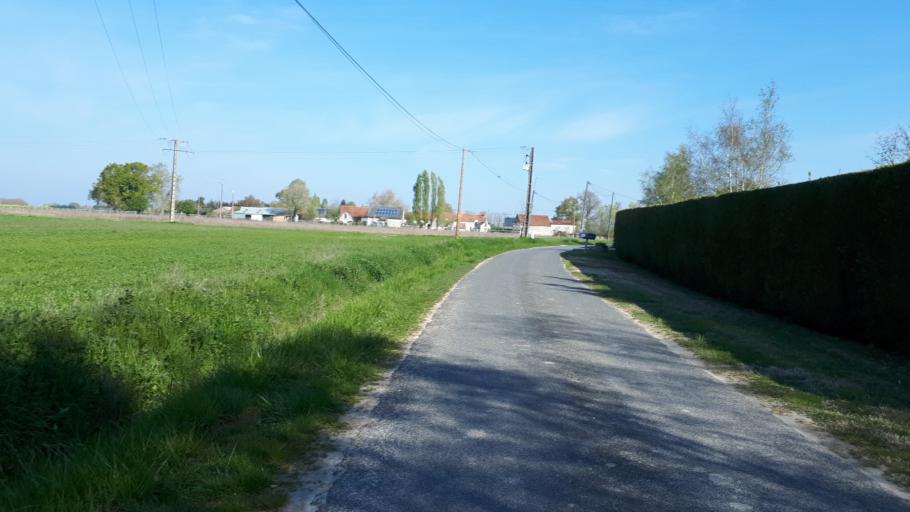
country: FR
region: Centre
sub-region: Departement du Loir-et-Cher
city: Contres
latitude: 47.3784
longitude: 1.3939
